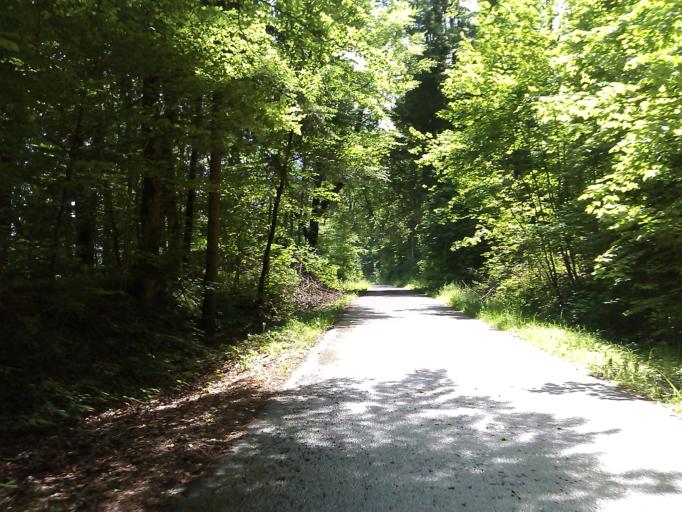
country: DE
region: Bavaria
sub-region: Swabia
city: Biessenhofen
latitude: 47.8574
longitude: 10.6315
